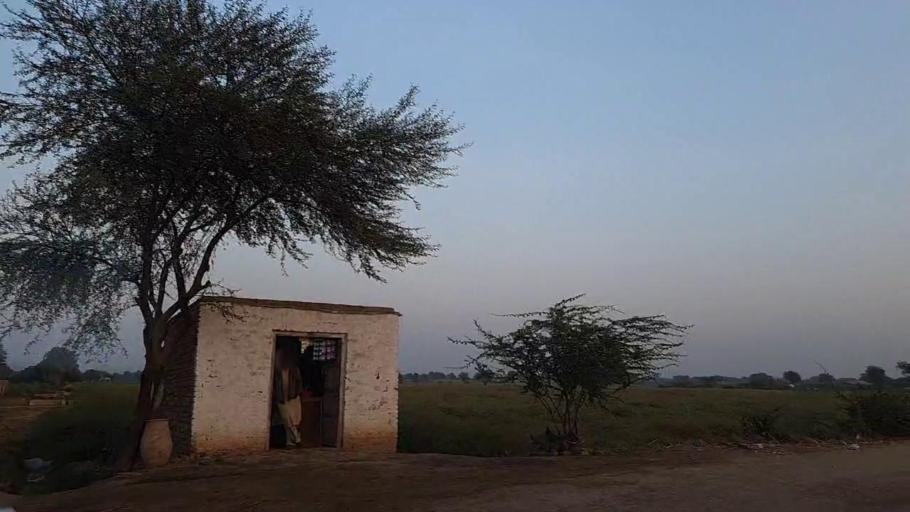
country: PK
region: Sindh
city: Tando Ghulam Ali
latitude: 25.1572
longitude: 68.9328
